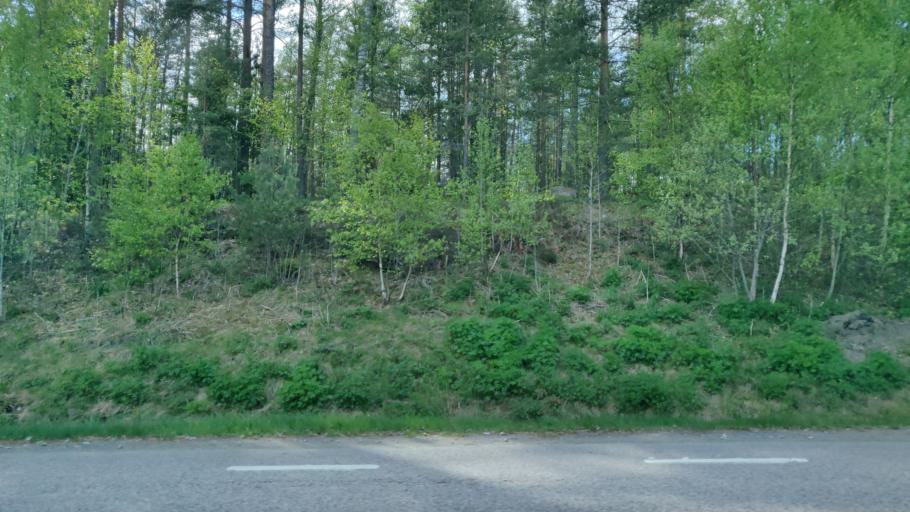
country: SE
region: Vaermland
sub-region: Hammaro Kommun
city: Skoghall
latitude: 59.3804
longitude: 13.4045
